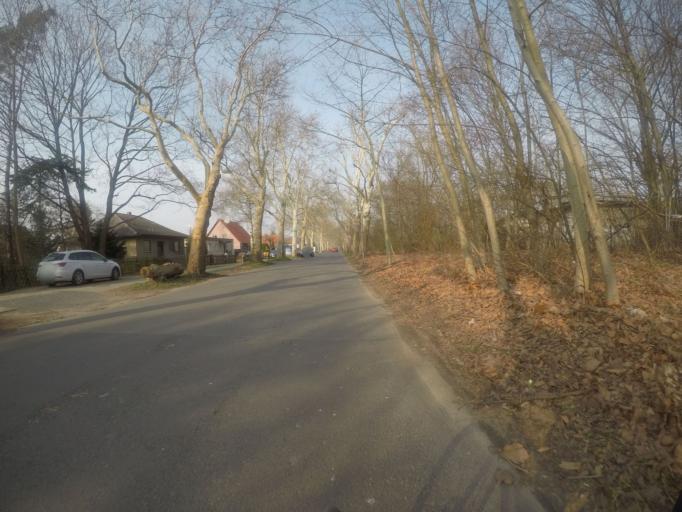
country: DE
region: Berlin
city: Rudow
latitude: 52.4043
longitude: 13.4903
